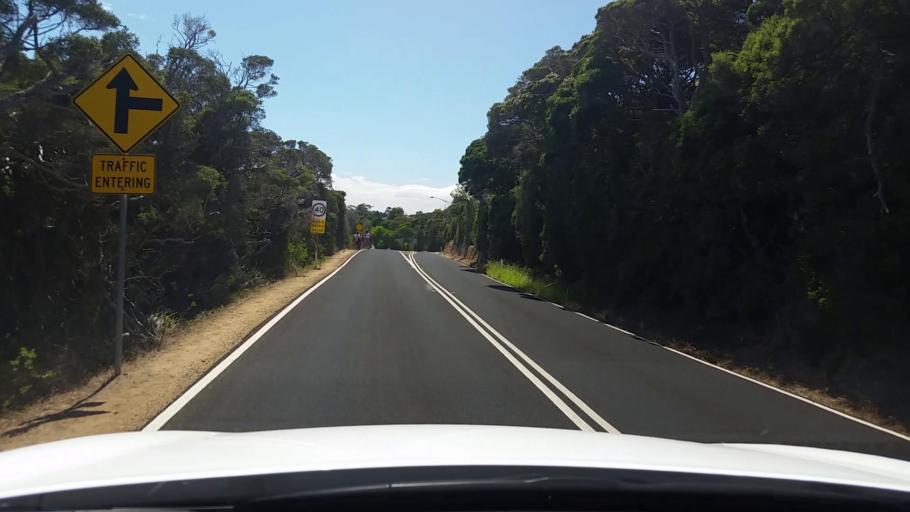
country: AU
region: Victoria
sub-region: Mornington Peninsula
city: Mount Martha
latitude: -38.2789
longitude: 144.9991
